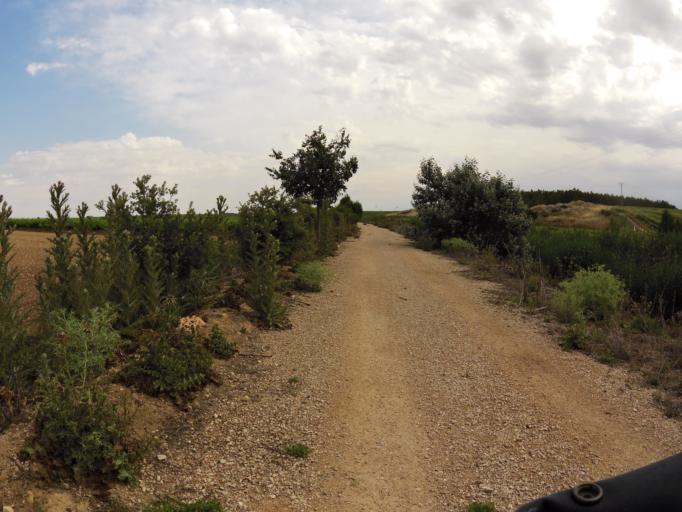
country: ES
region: Castille-La Mancha
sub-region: Provincia de Albacete
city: Albacete
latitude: 39.0516
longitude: -1.7572
